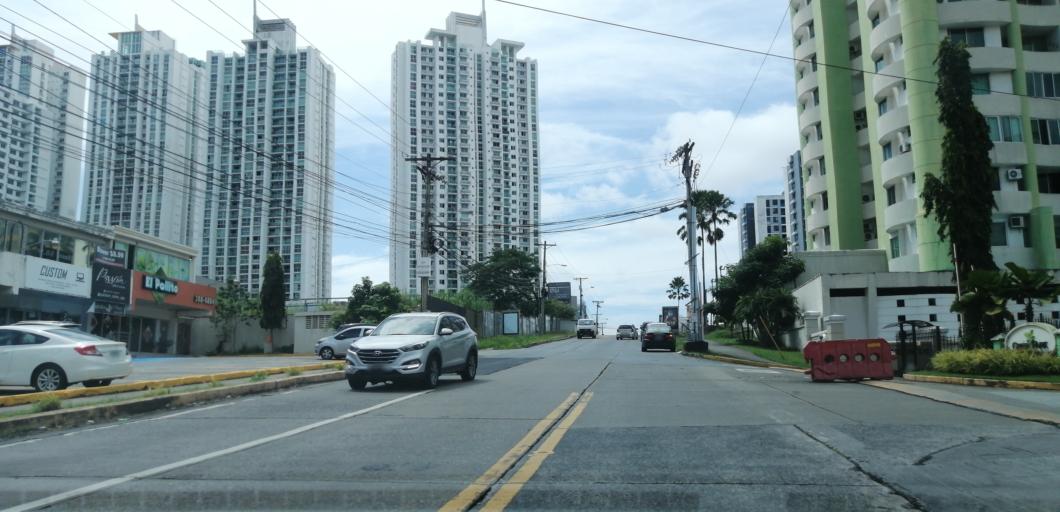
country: PA
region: Panama
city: Panama
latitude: 9.0286
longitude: -79.5249
